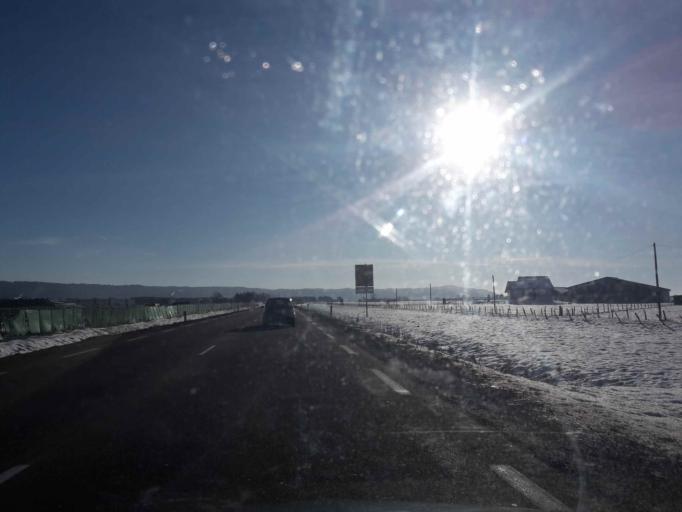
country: FR
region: Franche-Comte
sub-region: Departement du Doubs
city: Doubs
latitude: 46.9308
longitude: 6.3410
